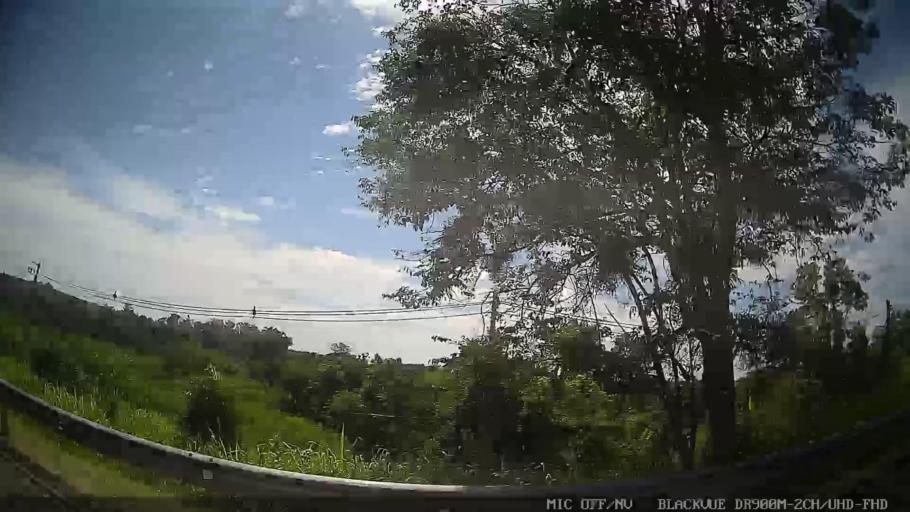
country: BR
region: Sao Paulo
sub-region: Porto Feliz
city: Porto Feliz
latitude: -23.2198
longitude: -47.5723
